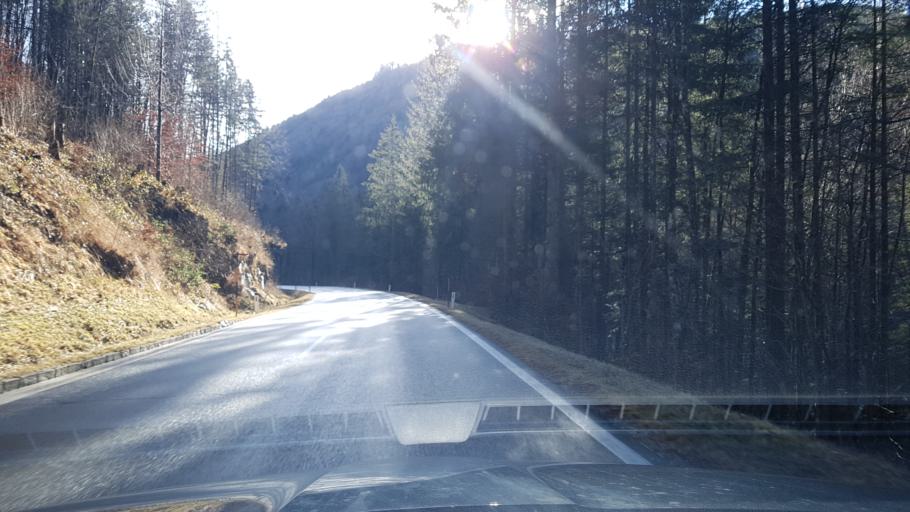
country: AT
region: Salzburg
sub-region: Politischer Bezirk Hallein
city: Krispl
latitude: 47.7353
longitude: 13.1626
